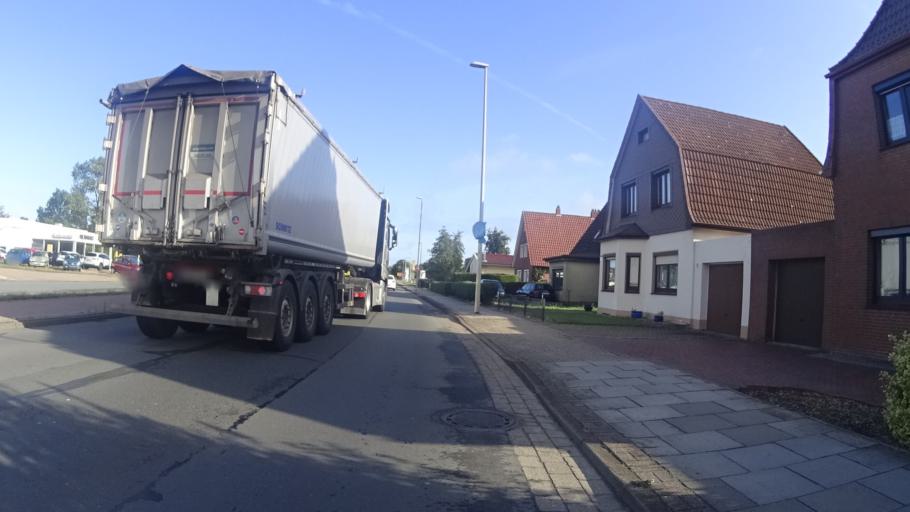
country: DE
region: Lower Saxony
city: Nordenham
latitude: 53.5013
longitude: 8.4785
